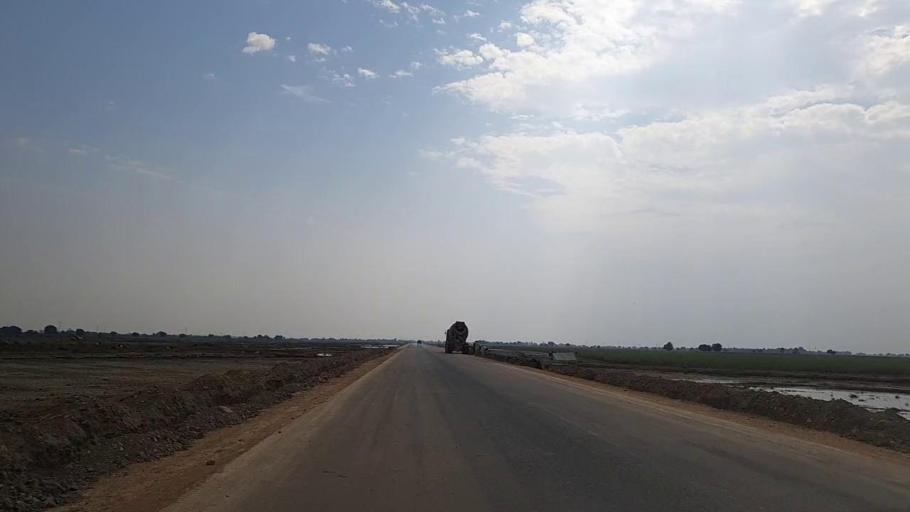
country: PK
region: Sindh
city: Naukot
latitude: 24.9984
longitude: 69.2854
